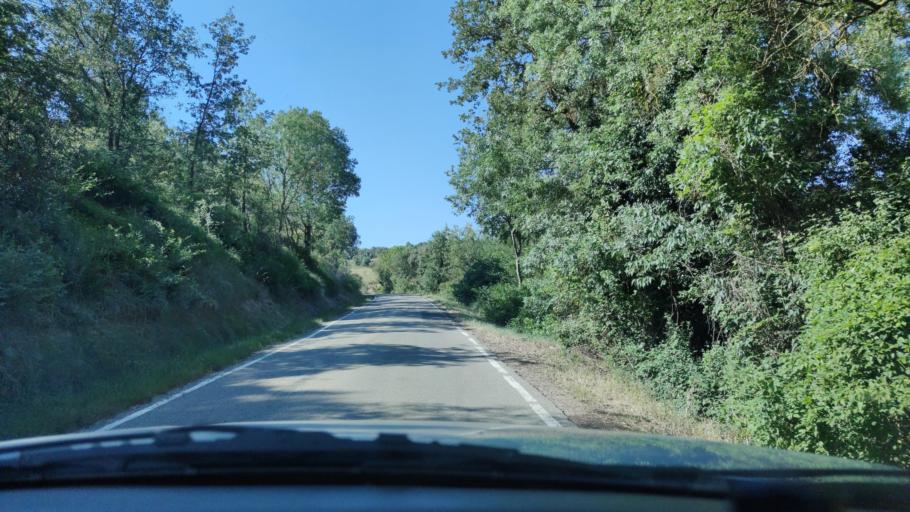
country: ES
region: Catalonia
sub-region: Provincia de Lleida
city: Sant Guim de Freixenet
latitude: 41.6776
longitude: 1.4040
